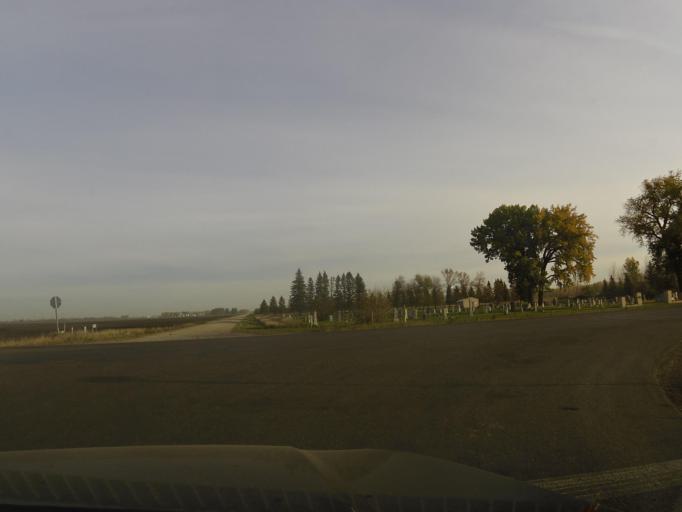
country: US
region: North Dakota
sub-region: Walsh County
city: Grafton
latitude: 48.5710
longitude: -97.1904
